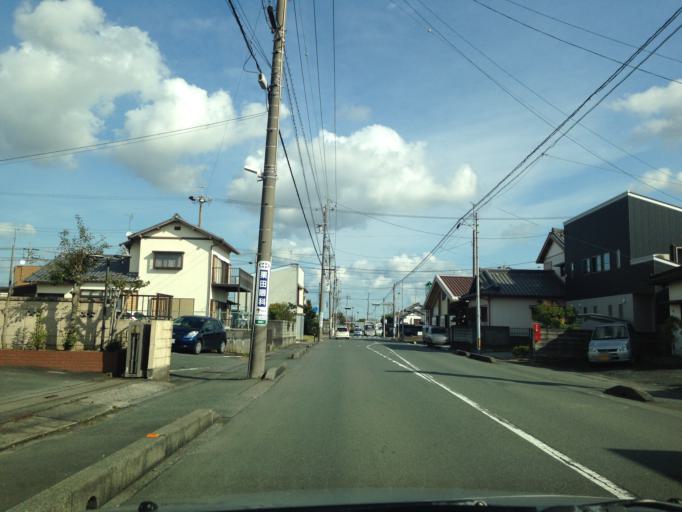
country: JP
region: Shizuoka
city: Fukuroi
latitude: 34.7544
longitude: 137.9224
